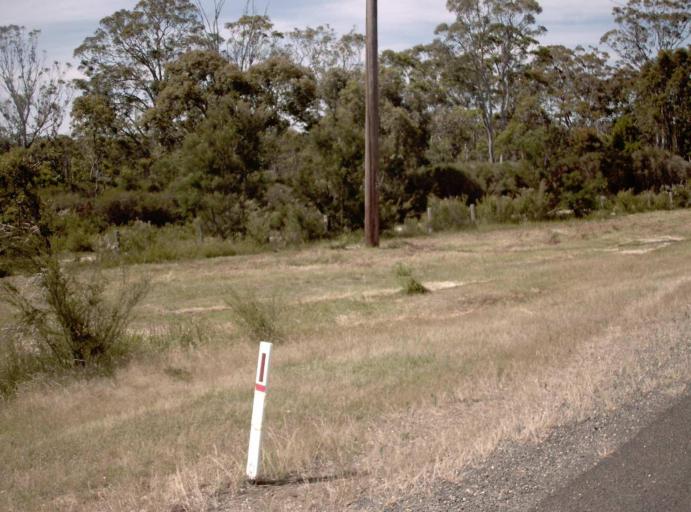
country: AU
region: Victoria
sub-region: East Gippsland
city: Bairnsdale
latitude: -37.9098
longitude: 147.3159
